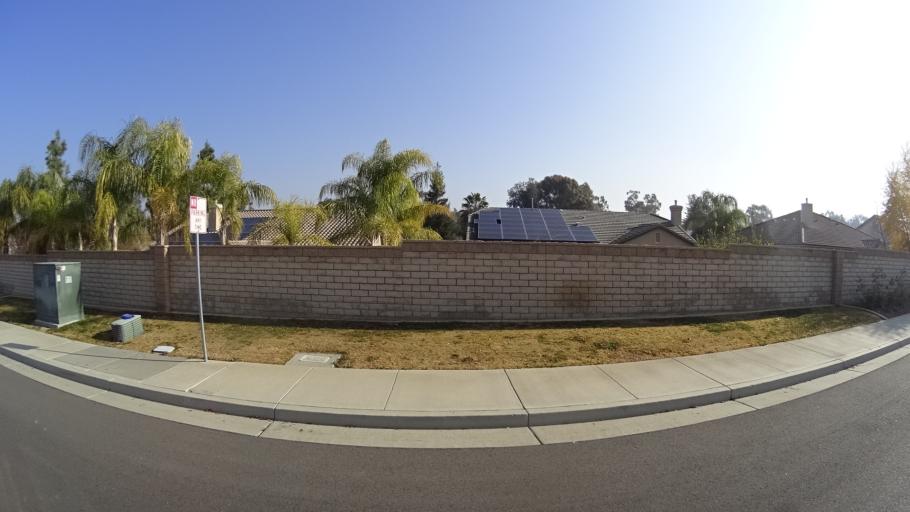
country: US
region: California
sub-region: Kern County
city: Lamont
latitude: 35.4007
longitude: -118.8454
